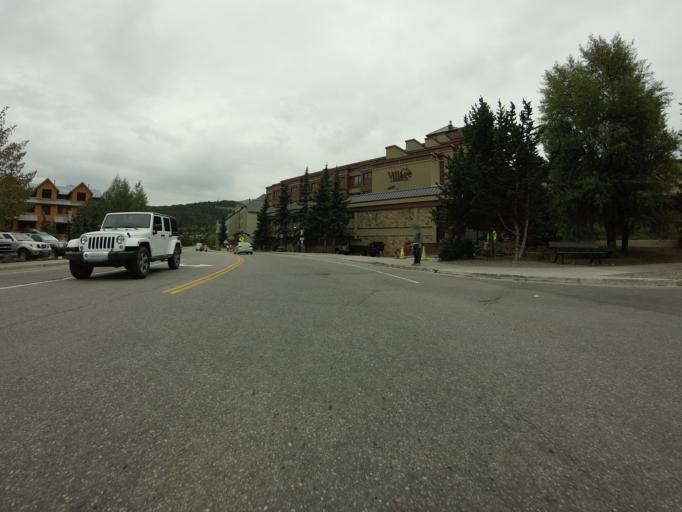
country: US
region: Colorado
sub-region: Summit County
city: Breckenridge
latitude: 39.4777
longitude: -106.0476
